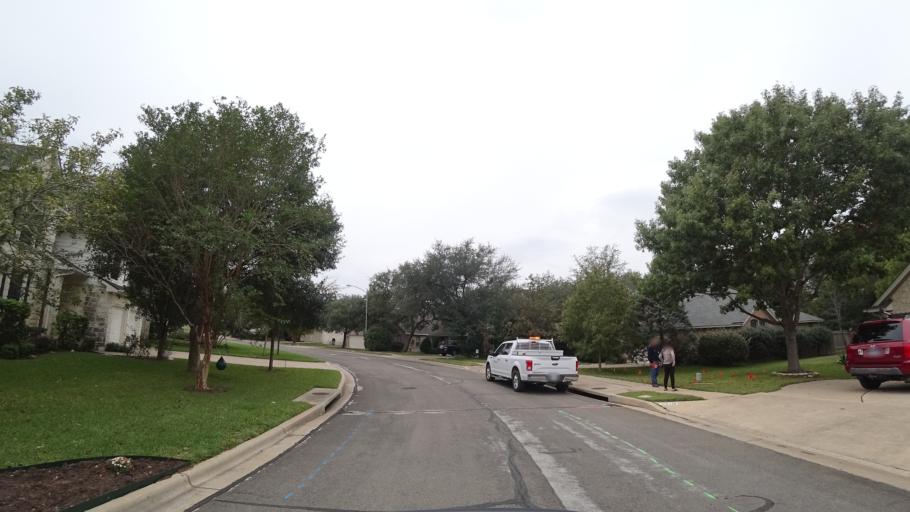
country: US
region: Texas
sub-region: Travis County
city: Shady Hollow
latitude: 30.2104
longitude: -97.8828
